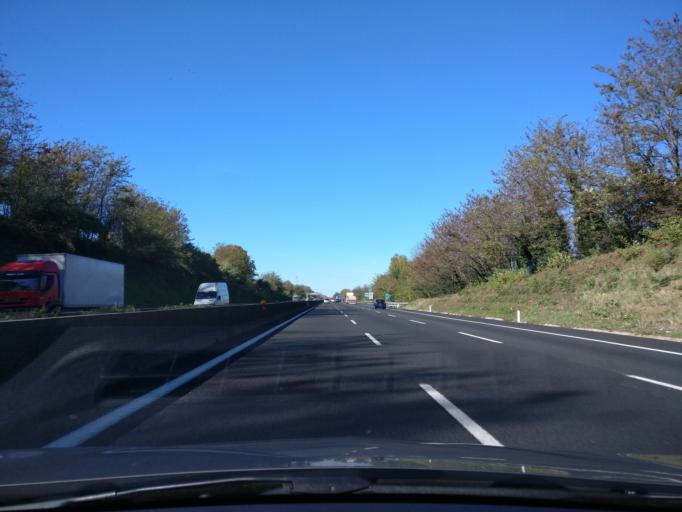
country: IT
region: Latium
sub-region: Citta metropolitana di Roma Capitale
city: Valmontone
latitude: 41.7717
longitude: 12.8996
